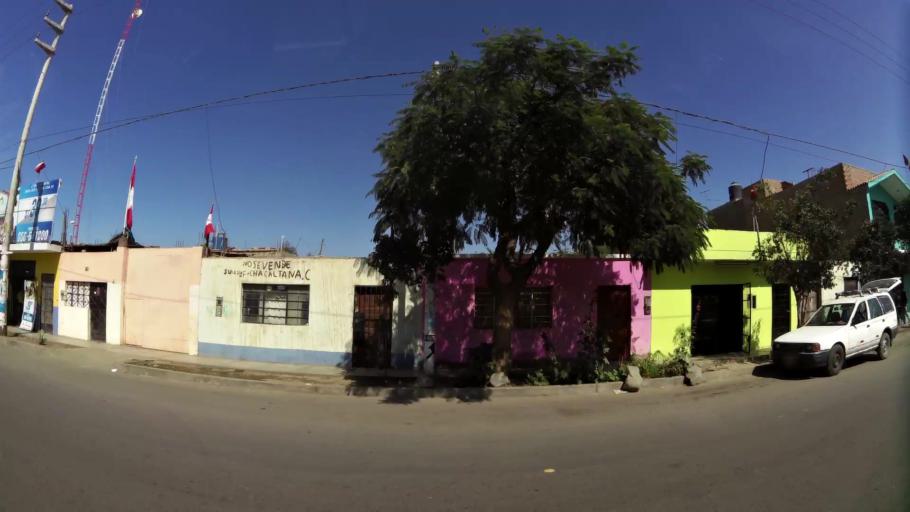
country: PE
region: Ica
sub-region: Provincia de Ica
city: La Tinguina
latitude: -14.0456
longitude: -75.7076
